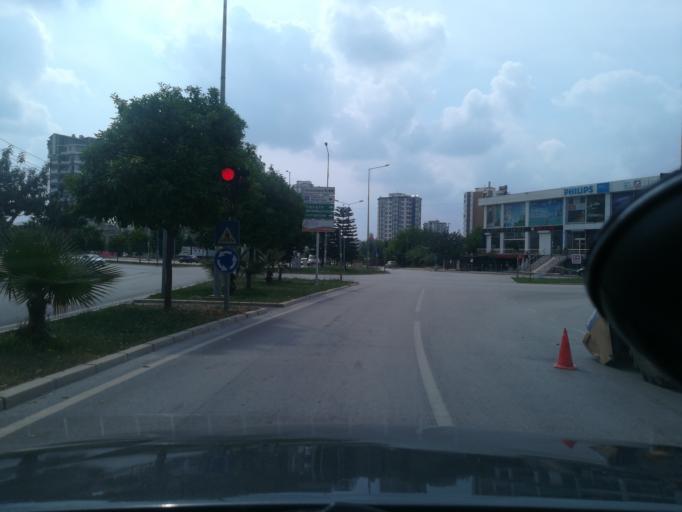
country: TR
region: Adana
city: Seyhan
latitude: 37.0216
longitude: 35.2636
